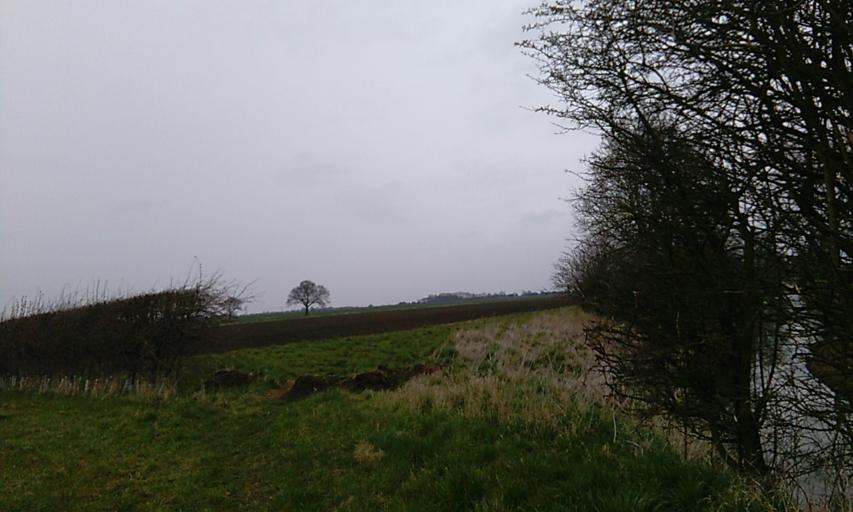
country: GB
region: England
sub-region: Nottinghamshire
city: Bingham
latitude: 52.9238
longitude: -0.9335
